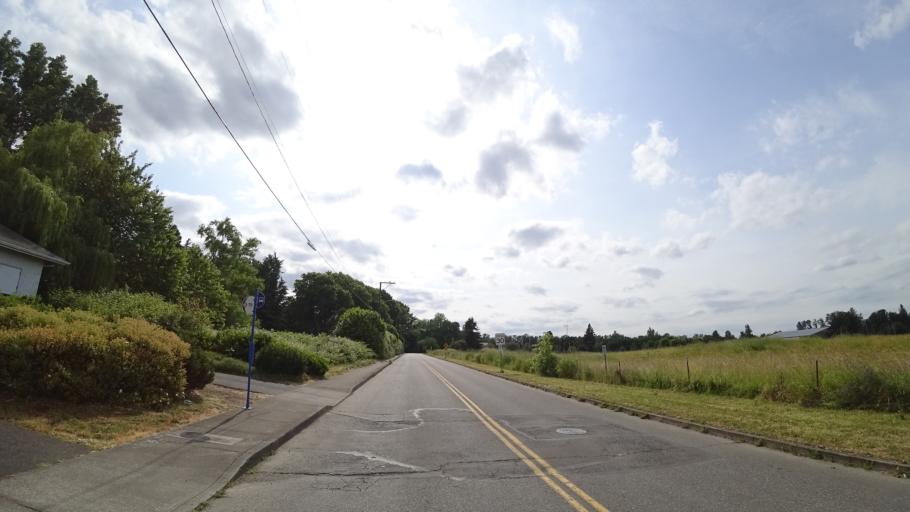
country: US
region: Washington
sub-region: Clark County
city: Vancouver
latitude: 45.5894
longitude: -122.6327
